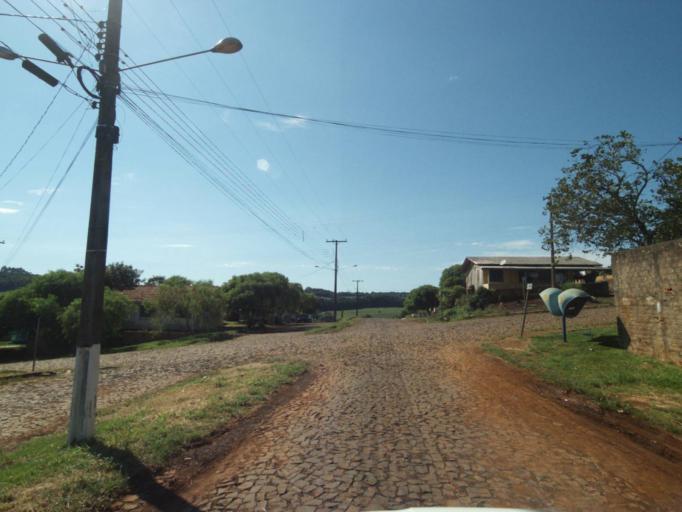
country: BR
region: Parana
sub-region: Laranjeiras Do Sul
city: Laranjeiras do Sul
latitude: -25.4928
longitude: -52.5250
